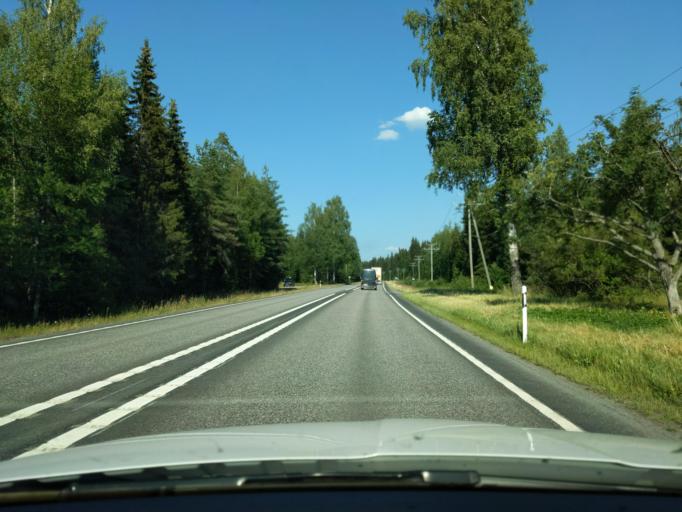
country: FI
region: Paijanne Tavastia
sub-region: Lahti
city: Hollola
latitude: 60.9384
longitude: 25.3953
